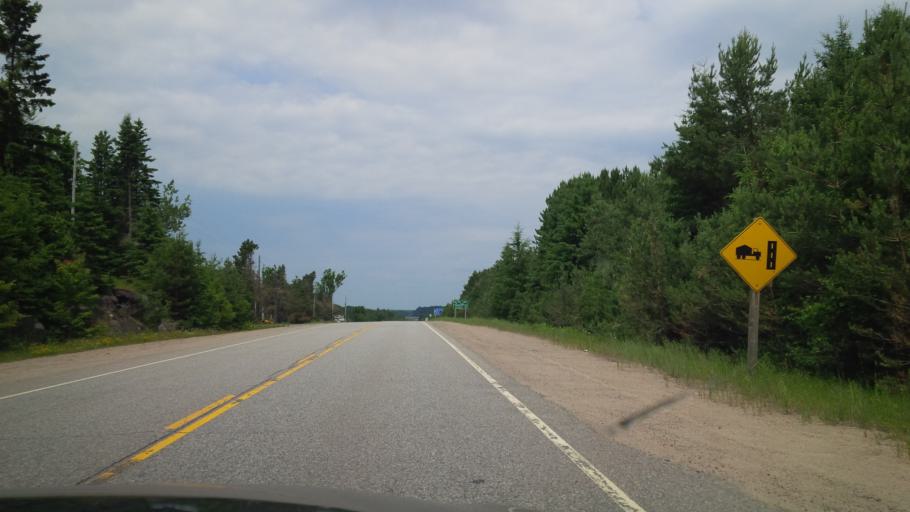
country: CA
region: Ontario
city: Huntsville
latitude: 45.5232
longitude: -79.3165
